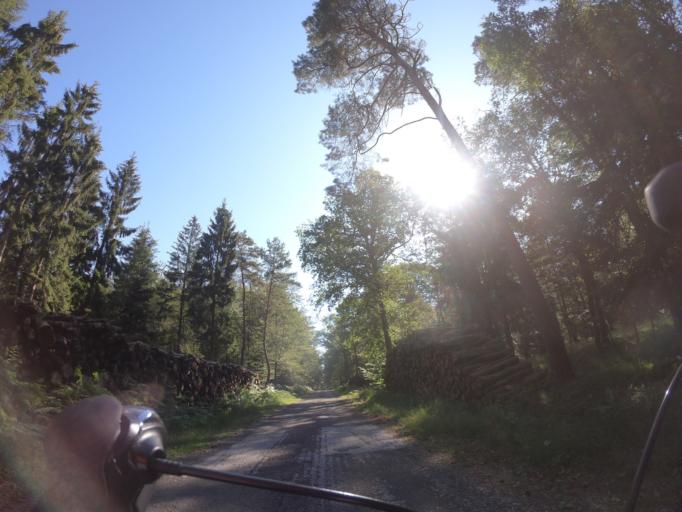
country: FR
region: Lower Normandy
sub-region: Departement de l'Orne
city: Juvigny-sous-Andaine
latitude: 48.5857
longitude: -0.5006
